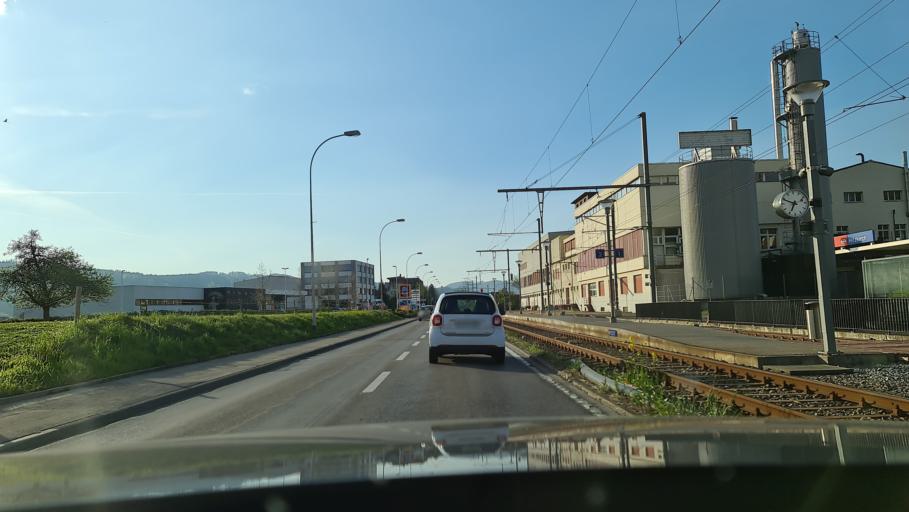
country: CH
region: Lucerne
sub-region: Hochdorf District
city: Hitzkirch
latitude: 47.2223
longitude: 8.2522
